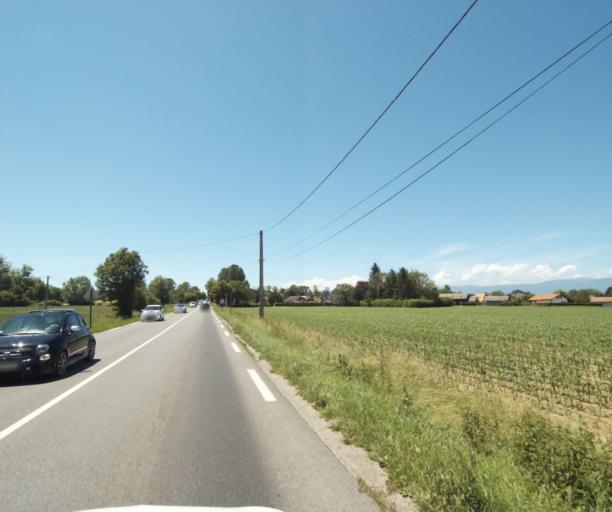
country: FR
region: Rhone-Alpes
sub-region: Departement de la Haute-Savoie
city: Sciez
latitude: 46.3285
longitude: 6.3632
